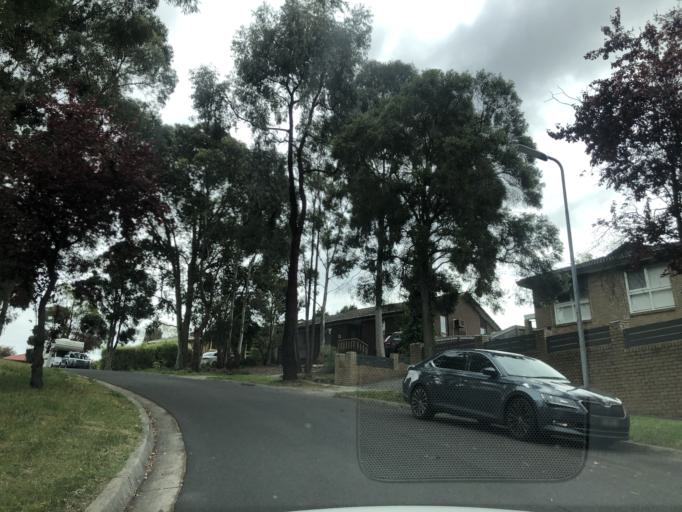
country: AU
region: Victoria
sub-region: Greater Dandenong
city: Noble Park North
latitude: -37.9360
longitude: 145.2018
